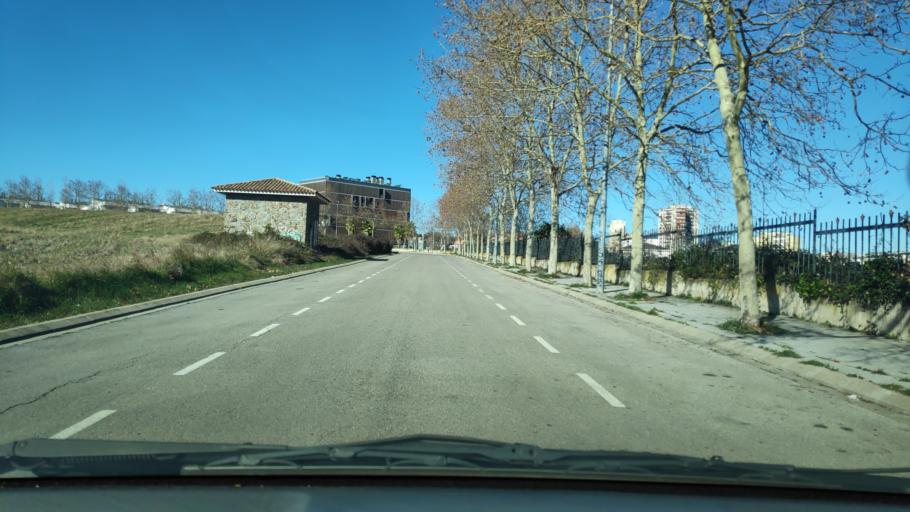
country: ES
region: Catalonia
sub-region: Provincia de Barcelona
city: Sant Quirze del Valles
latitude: 41.5390
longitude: 2.0912
